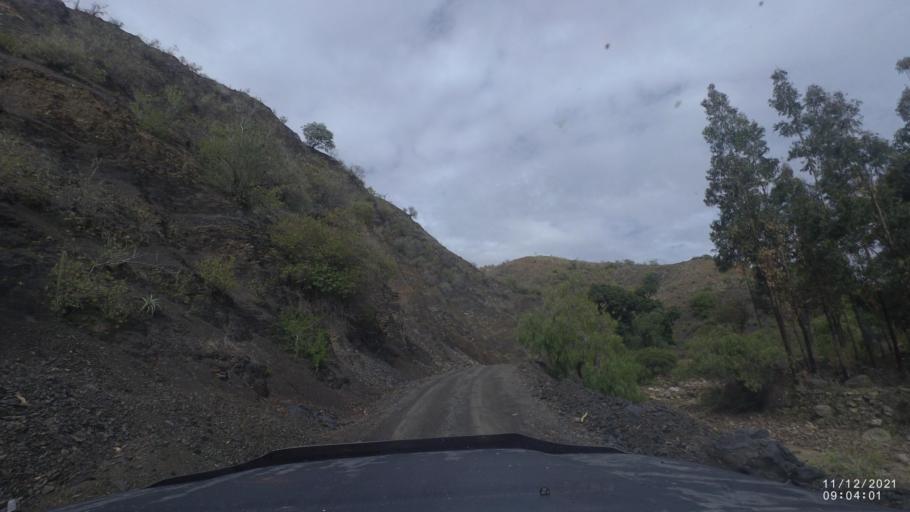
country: BO
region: Cochabamba
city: Tarata
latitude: -17.8952
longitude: -65.9492
